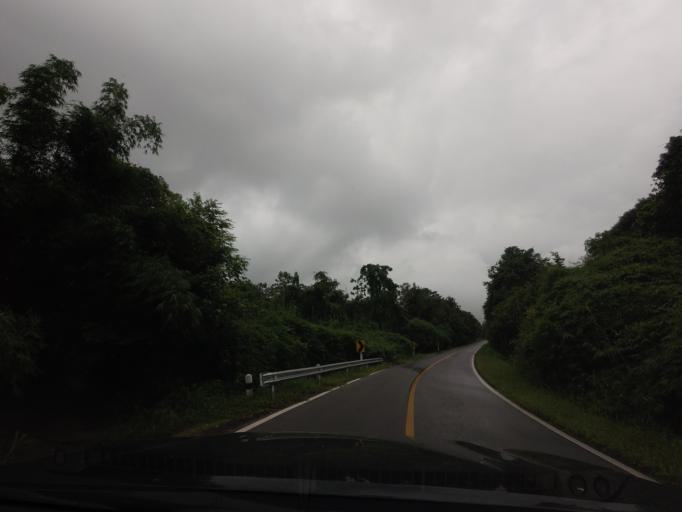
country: TH
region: Nong Khai
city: Sangkhom
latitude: 18.0273
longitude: 102.3437
